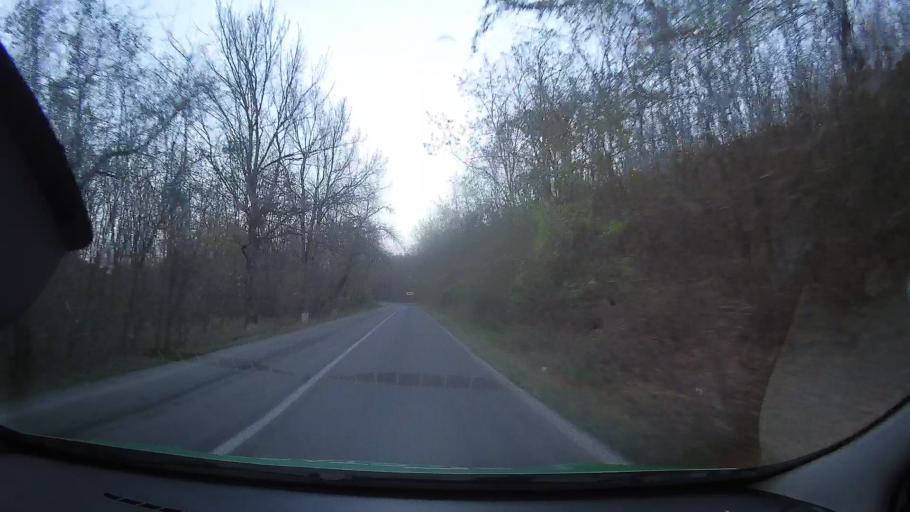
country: RO
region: Constanta
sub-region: Comuna Baneasa
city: Baneasa
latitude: 44.0812
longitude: 27.6672
